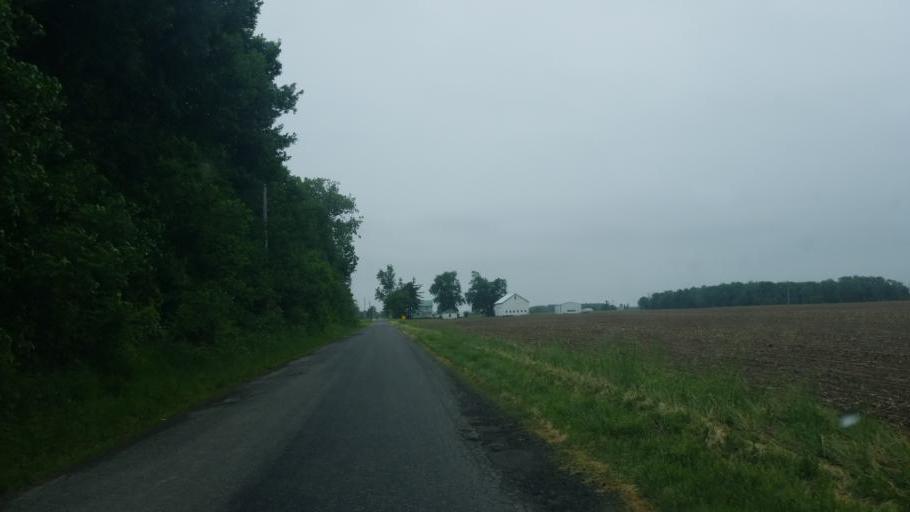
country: US
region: Indiana
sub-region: Marshall County
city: Bremen
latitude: 41.5047
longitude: -86.1370
